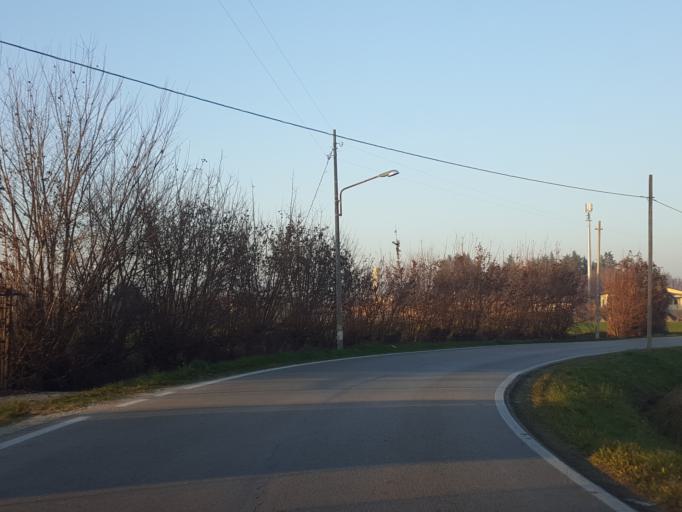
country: IT
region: Veneto
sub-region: Provincia di Vicenza
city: Villaggio Montegrappa
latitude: 45.5528
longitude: 11.6027
